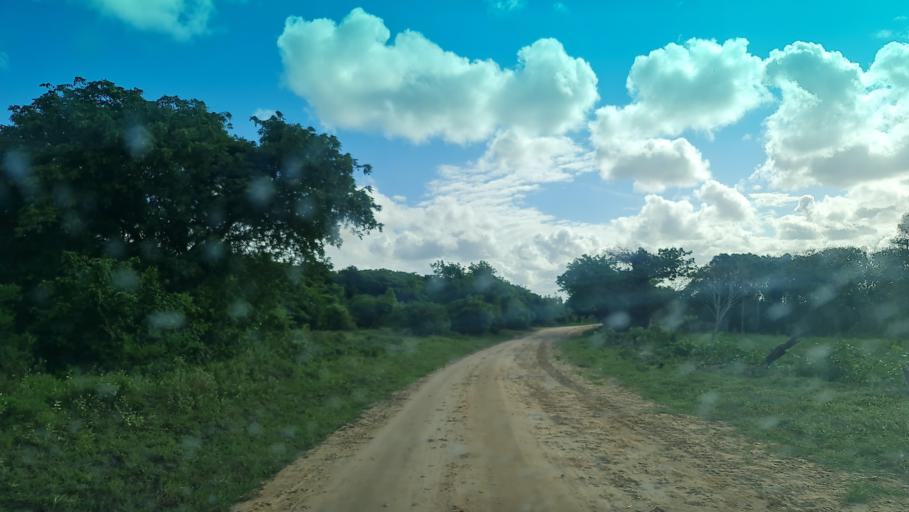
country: MZ
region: Maputo
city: Manhica
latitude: -25.4364
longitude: 32.8831
